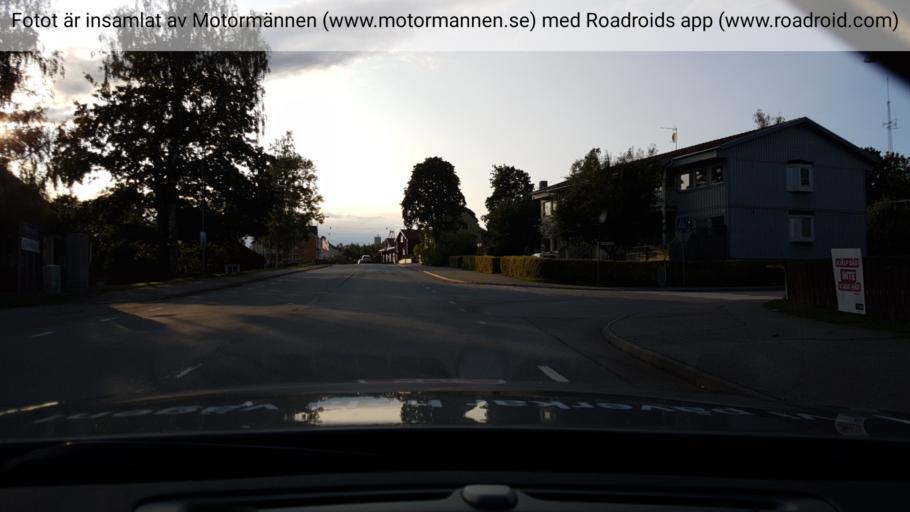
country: SE
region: OErebro
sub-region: Ljusnarsbergs Kommun
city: Kopparberg
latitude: 59.8745
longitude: 15.0008
